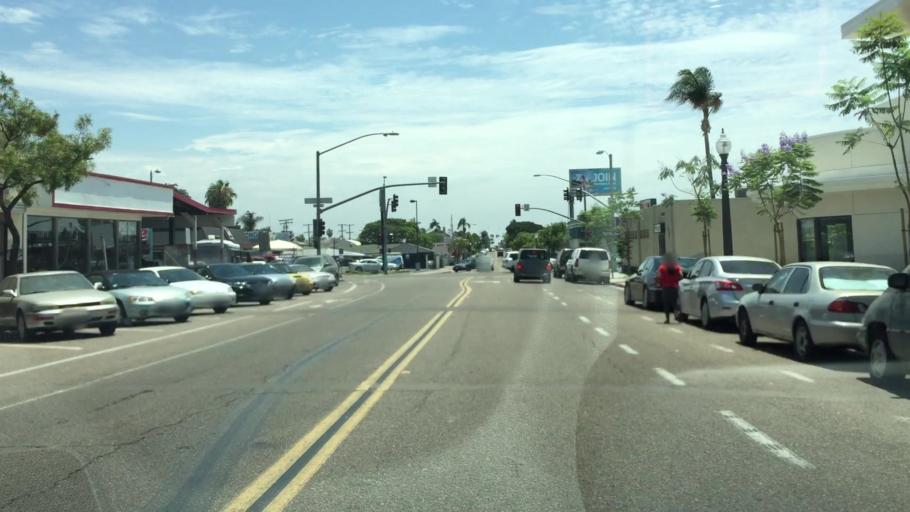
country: US
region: California
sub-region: San Diego County
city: Lemon Grove
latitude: 32.7568
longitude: -117.0922
